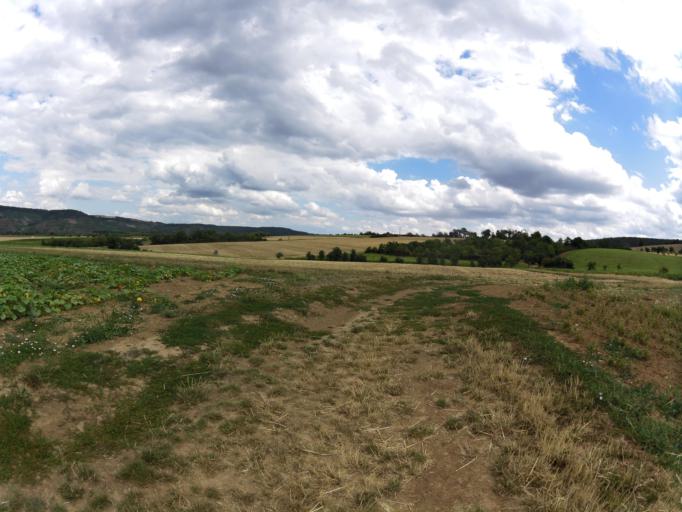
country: DE
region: Bavaria
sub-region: Regierungsbezirk Unterfranken
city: Zellingen
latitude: 49.8760
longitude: 9.8168
